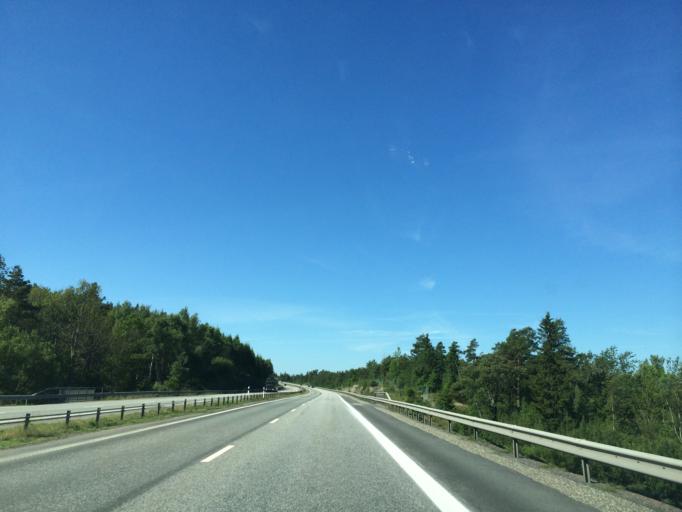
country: SE
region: Joenkoeping
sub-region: Jonkopings Kommun
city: Graenna
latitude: 57.9659
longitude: 14.3628
